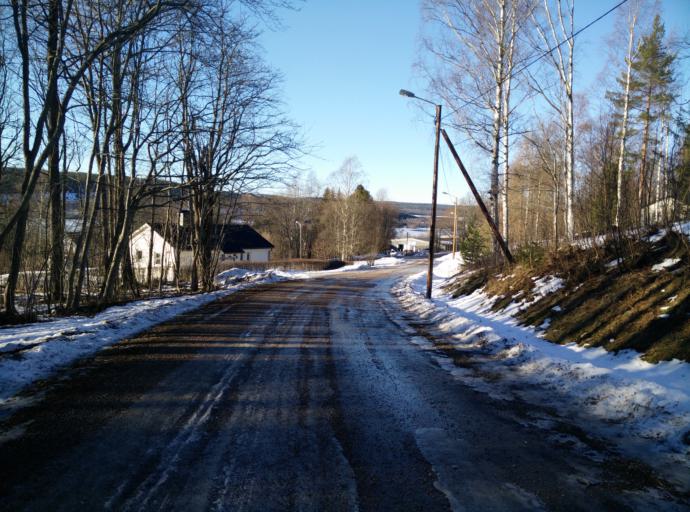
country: SE
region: Vaesternorrland
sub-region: Sundsvalls Kommun
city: Skottsund
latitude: 62.3132
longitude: 17.3970
